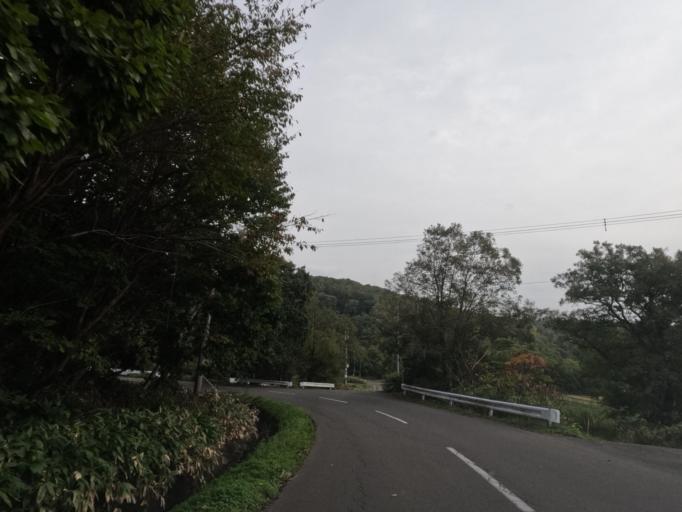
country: JP
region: Hokkaido
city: Date
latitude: 42.4012
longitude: 140.9248
